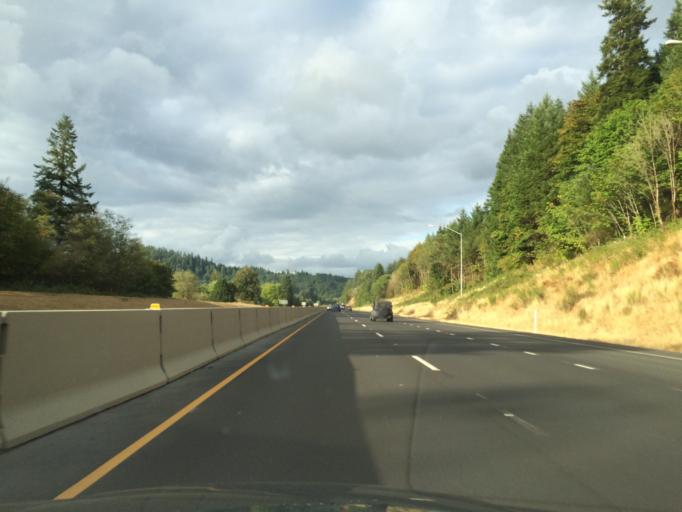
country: US
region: Oregon
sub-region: Douglas County
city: Drain
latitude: 43.7251
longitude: -123.2052
